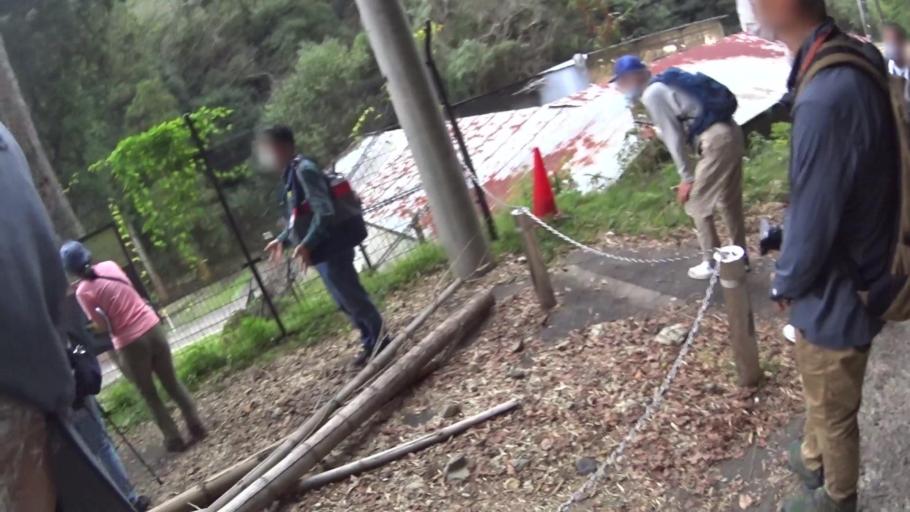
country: JP
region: Osaka
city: Kaizuka
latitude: 34.4645
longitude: 135.2971
